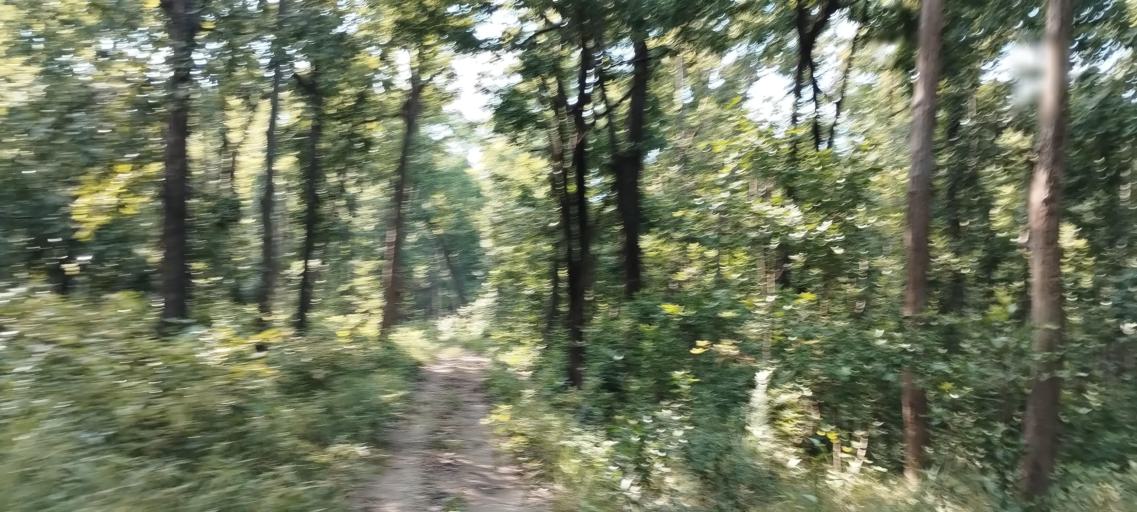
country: NP
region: Far Western
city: Tikapur
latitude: 28.5228
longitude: 81.2632
